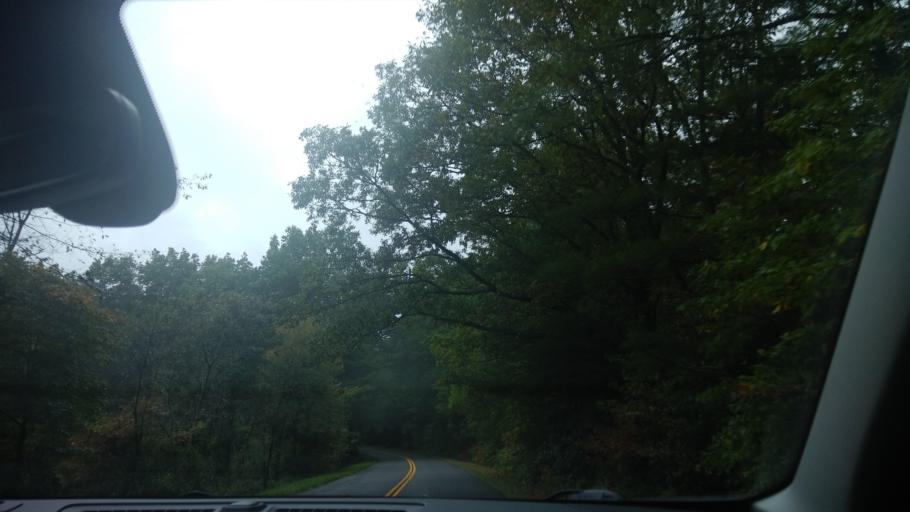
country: US
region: North Carolina
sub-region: Mitchell County
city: Spruce Pine
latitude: 35.8863
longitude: -81.9809
